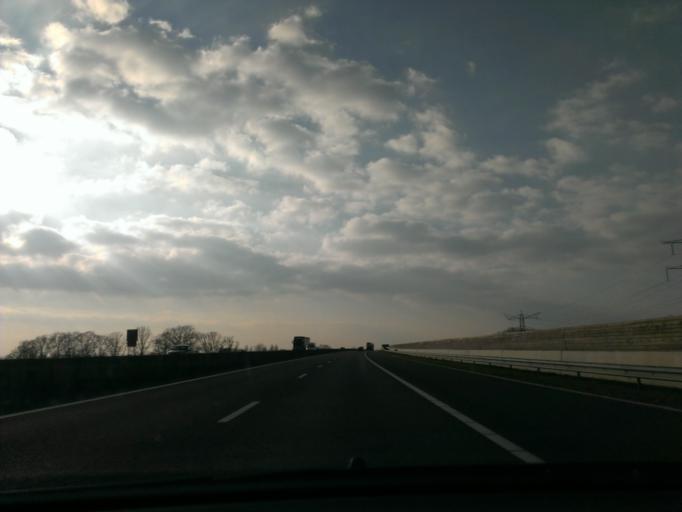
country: NL
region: Overijssel
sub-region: Gemeente Almelo
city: Almelo
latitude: 52.3255
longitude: 6.6329
